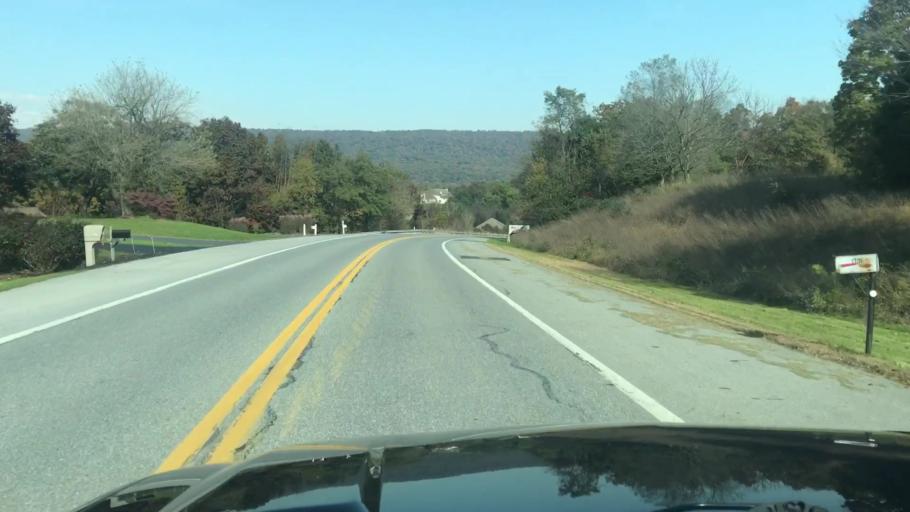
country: US
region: Pennsylvania
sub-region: Cumberland County
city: Enola
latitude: 40.2784
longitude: -76.9871
